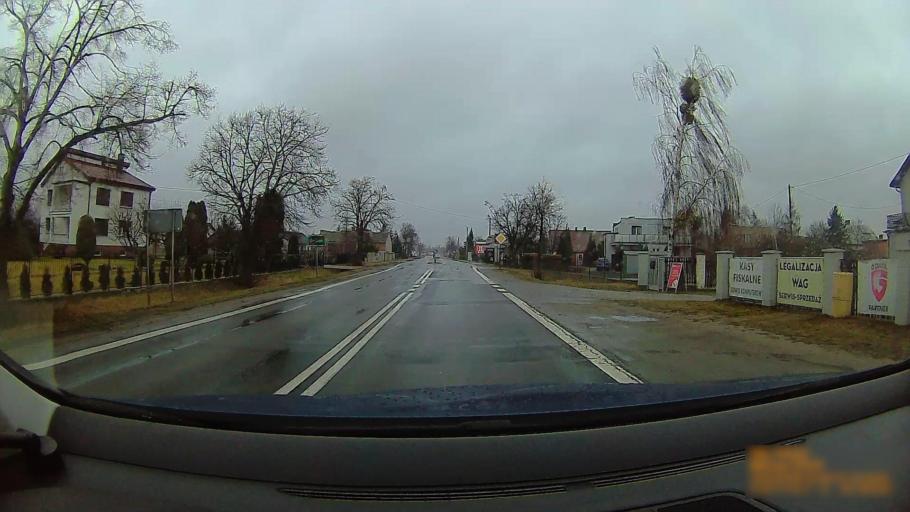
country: PL
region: Greater Poland Voivodeship
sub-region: Konin
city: Konin
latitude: 52.1871
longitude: 18.2670
